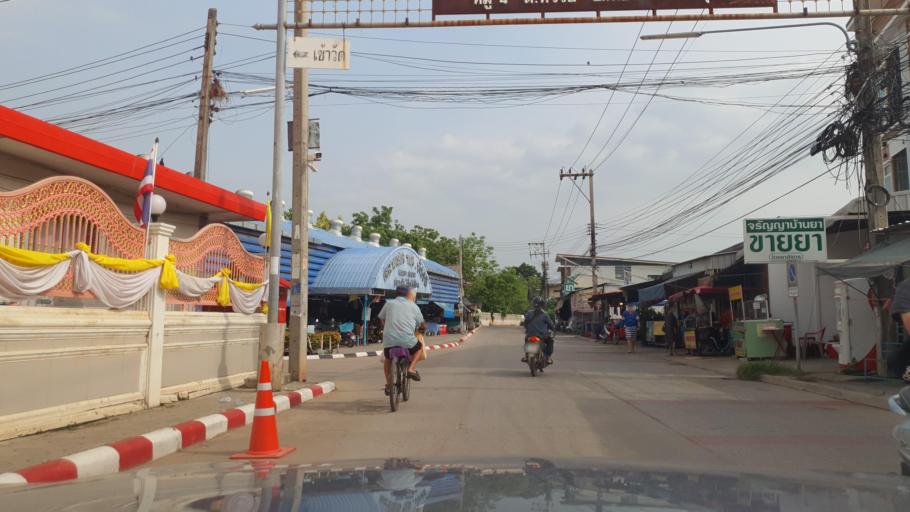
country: TH
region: Phitsanulok
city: Phitsanulok
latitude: 16.8480
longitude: 100.2567
